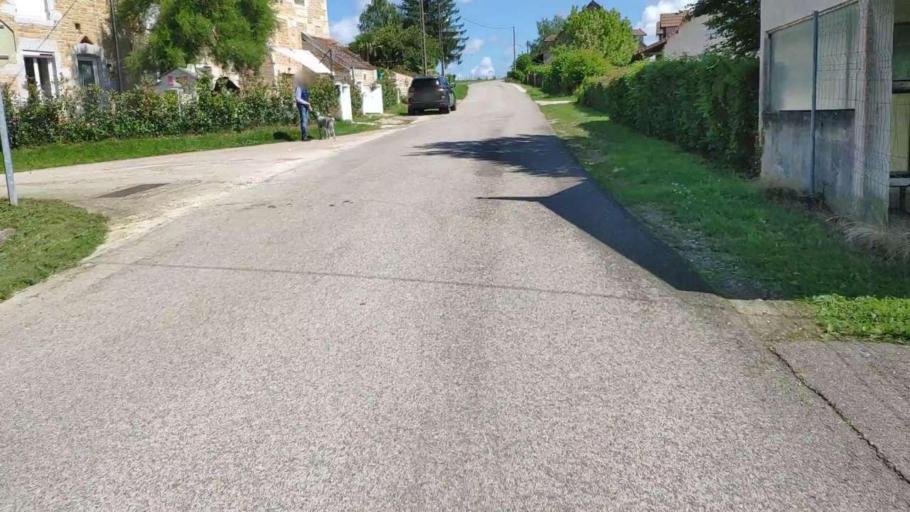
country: FR
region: Franche-Comte
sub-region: Departement du Jura
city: Bletterans
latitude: 46.8030
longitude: 5.5623
